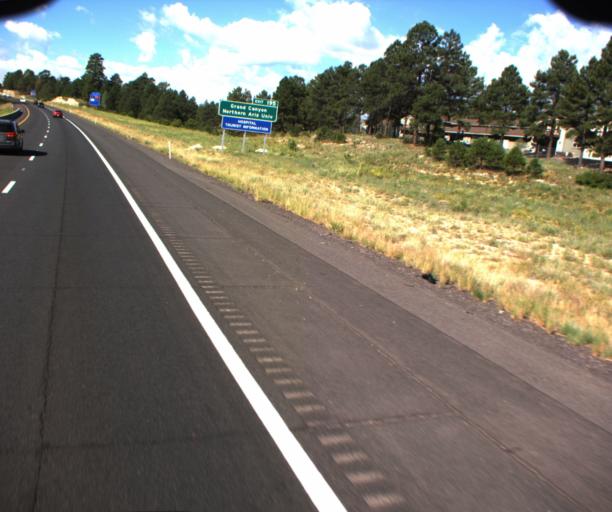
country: US
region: Arizona
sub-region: Coconino County
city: Flagstaff
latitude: 35.1836
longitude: -111.6366
